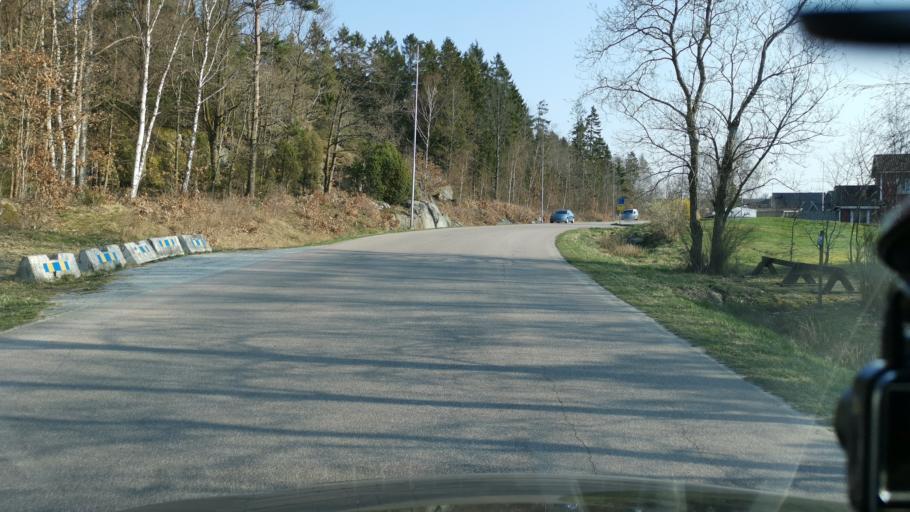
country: SE
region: Vaestra Goetaland
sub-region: Kungalvs Kommun
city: Kode
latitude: 57.9438
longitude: 11.8365
